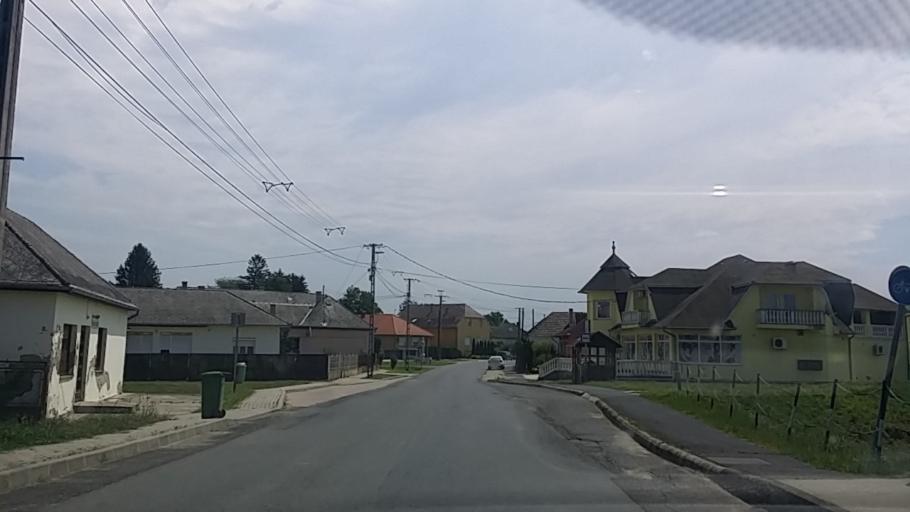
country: HR
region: Medimurska
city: Kotoriba
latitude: 46.3970
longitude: 16.8003
